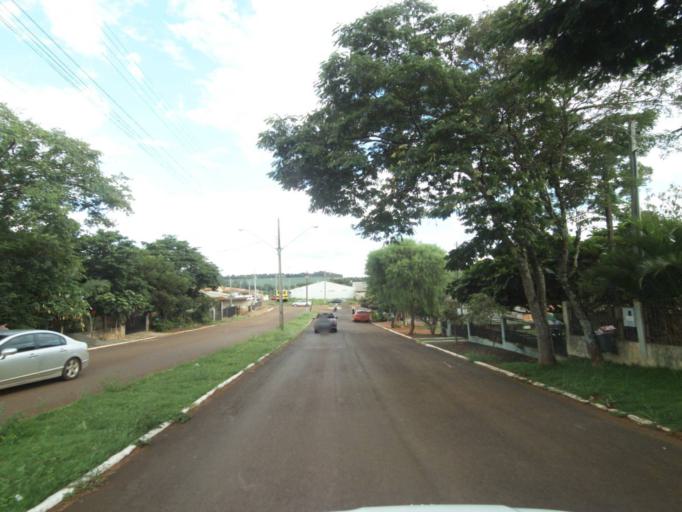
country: BR
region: Parana
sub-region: Laranjeiras Do Sul
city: Laranjeiras do Sul
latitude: -25.4948
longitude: -52.5273
